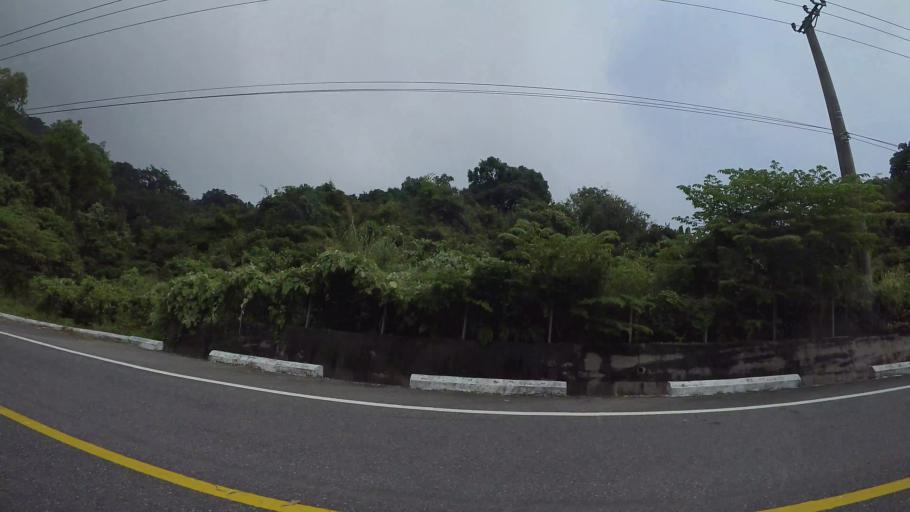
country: VN
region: Da Nang
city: Son Tra
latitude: 16.1018
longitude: 108.3038
